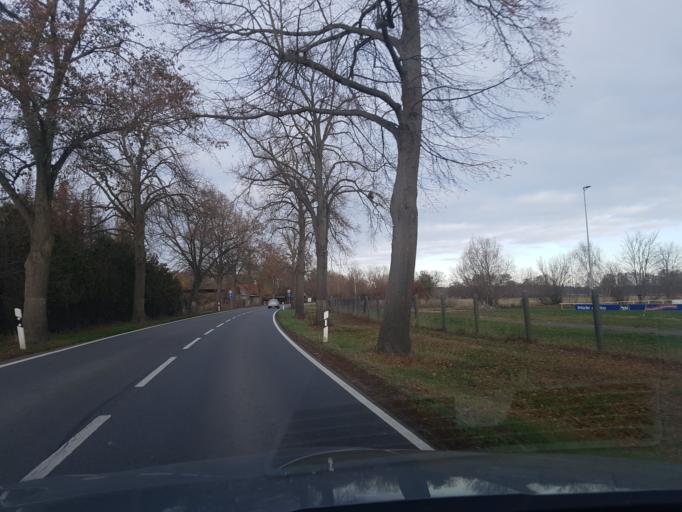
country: DE
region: Brandenburg
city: Golssen
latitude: 51.9646
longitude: 13.6167
